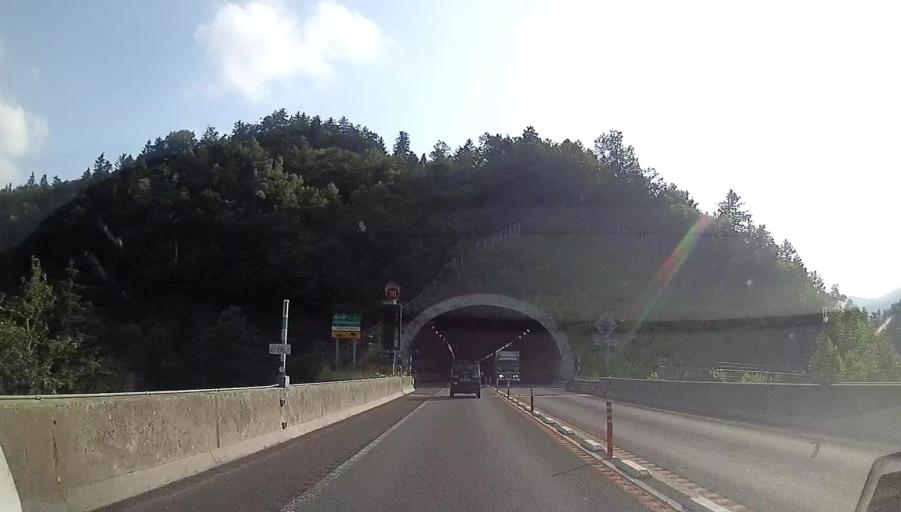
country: JP
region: Hokkaido
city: Shimo-furano
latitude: 43.0457
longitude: 142.4818
